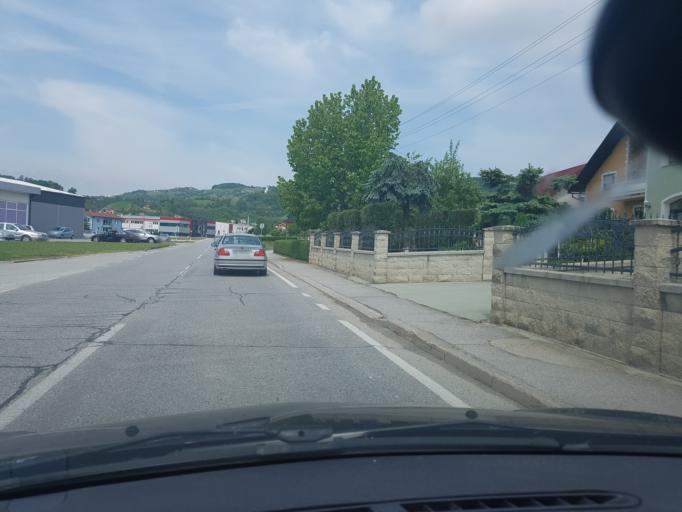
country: HR
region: Krapinsko-Zagorska
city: Pregrada
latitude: 46.1524
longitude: 15.7591
